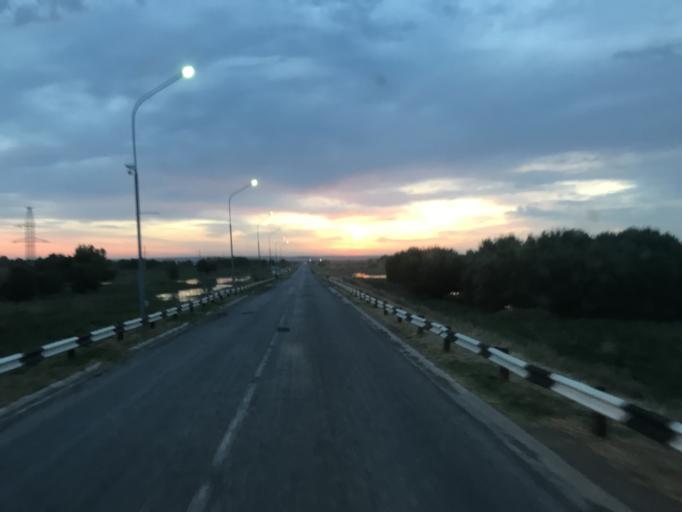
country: KZ
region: Ongtustik Qazaqstan
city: Ilyich
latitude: 41.0309
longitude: 68.5204
